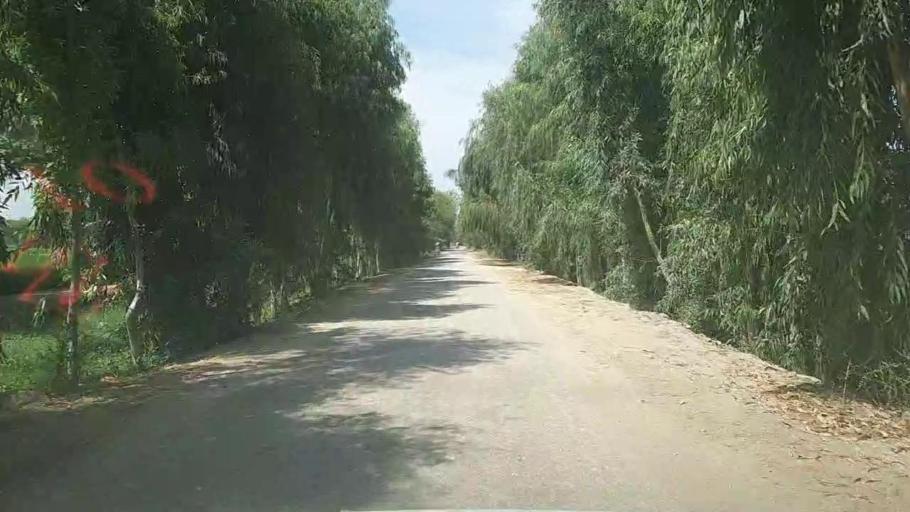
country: PK
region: Sindh
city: Kandhkot
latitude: 28.2966
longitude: 69.2366
